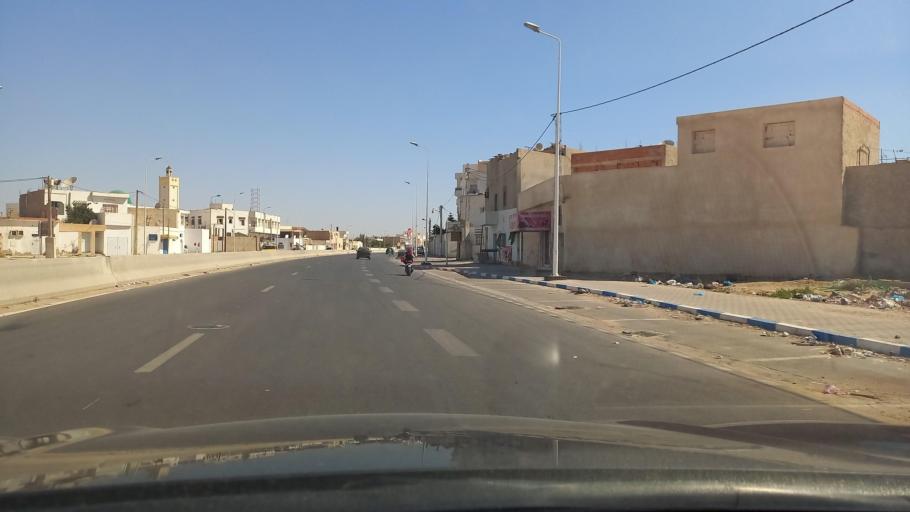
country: TN
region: Safaqis
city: Sfax
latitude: 34.7390
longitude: 10.7238
